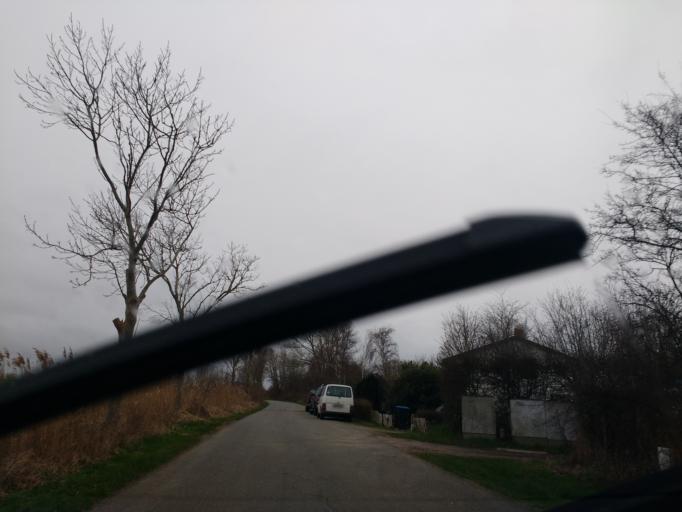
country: DE
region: Schleswig-Holstein
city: Grossenbrode
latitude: 54.3889
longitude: 11.1134
